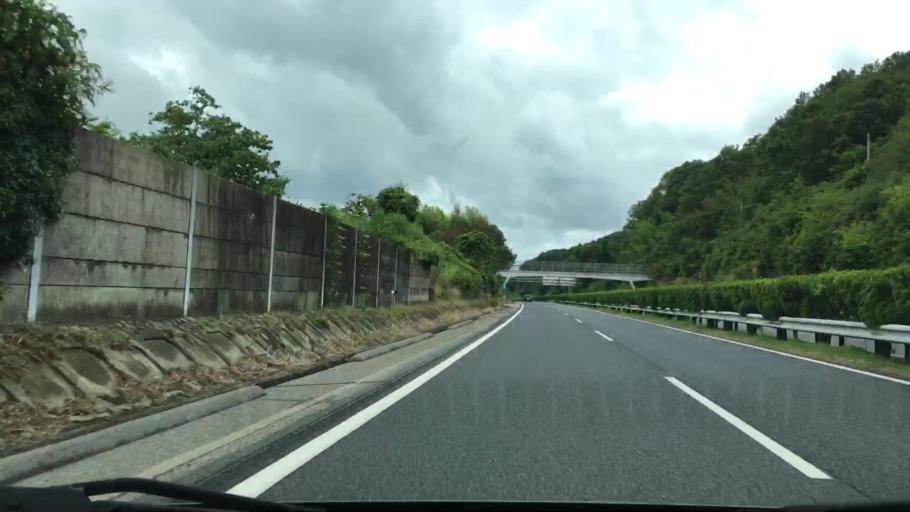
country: JP
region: Okayama
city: Tsuyama
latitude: 35.0398
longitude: 134.1277
